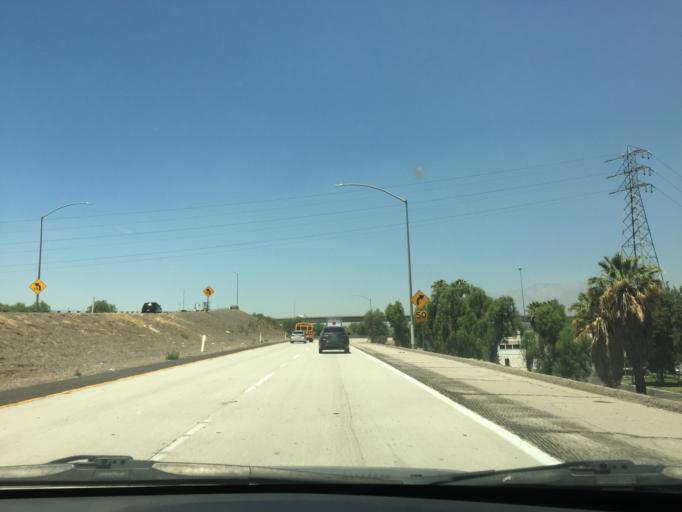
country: US
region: California
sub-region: San Bernardino County
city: Colton
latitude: 34.0642
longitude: -117.2916
